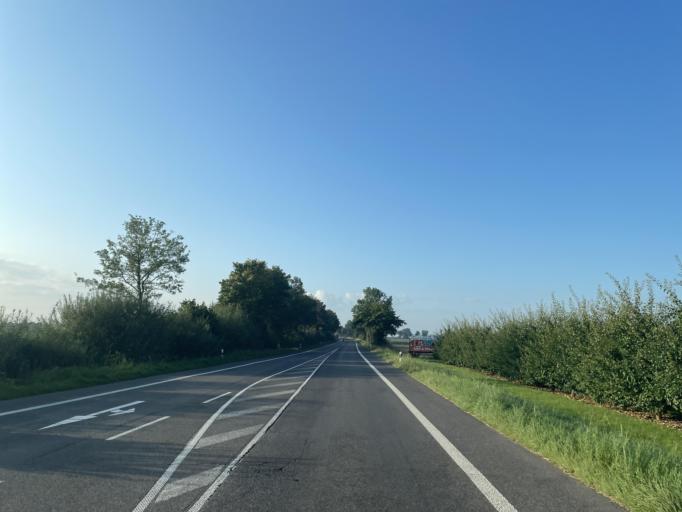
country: DE
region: North Rhine-Westphalia
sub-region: Regierungsbezirk Dusseldorf
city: Neubrueck
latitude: 51.1591
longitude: 6.5932
